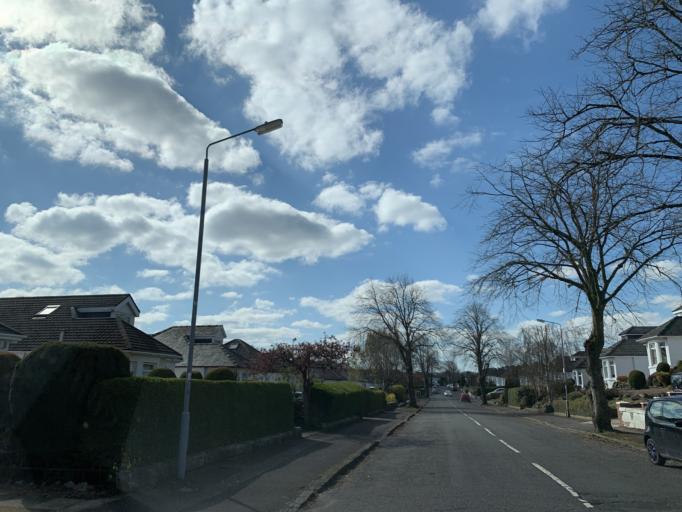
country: GB
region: Scotland
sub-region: East Renfrewshire
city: Clarkston
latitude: 55.7930
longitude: -4.2721
